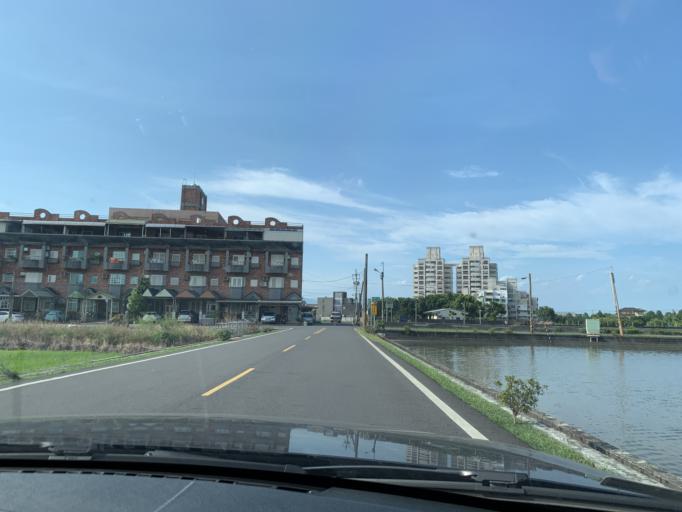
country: TW
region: Taiwan
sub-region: Yilan
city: Yilan
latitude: 24.6776
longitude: 121.8099
